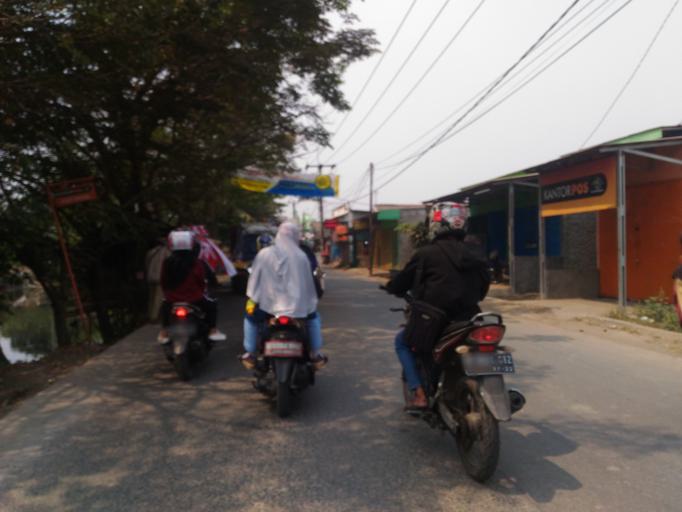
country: ID
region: West Java
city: Sepatan
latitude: -6.1465
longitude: 106.5622
